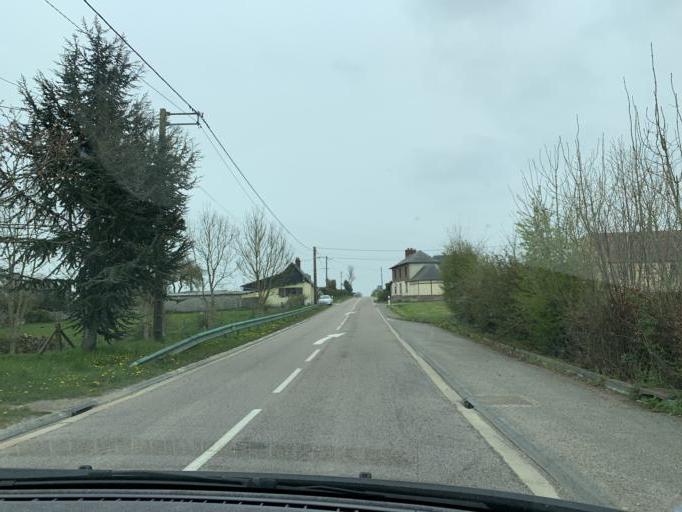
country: FR
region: Haute-Normandie
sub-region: Departement de la Seine-Maritime
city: Foucarmont
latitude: 49.8323
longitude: 1.5195
